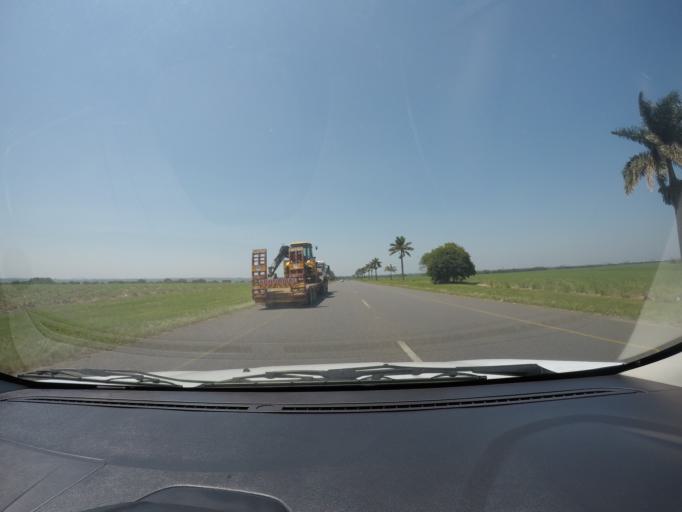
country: ZA
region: KwaZulu-Natal
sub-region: uThungulu District Municipality
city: Empangeni
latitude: -28.8081
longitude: 31.9566
